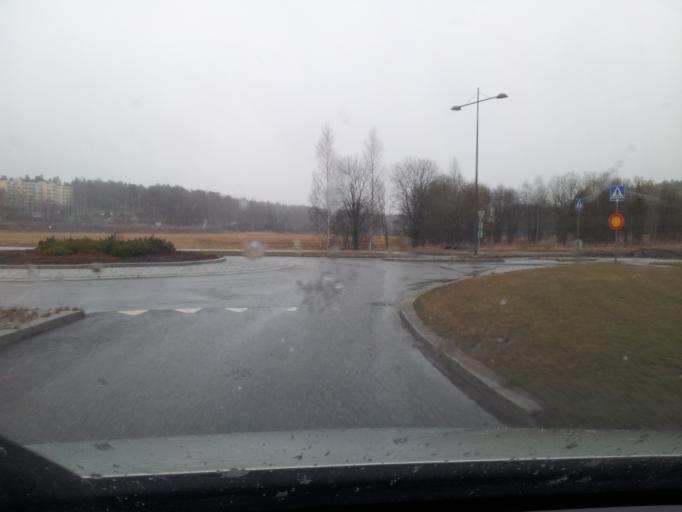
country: FI
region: Uusimaa
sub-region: Helsinki
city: Espoo
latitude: 60.1893
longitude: 24.6088
